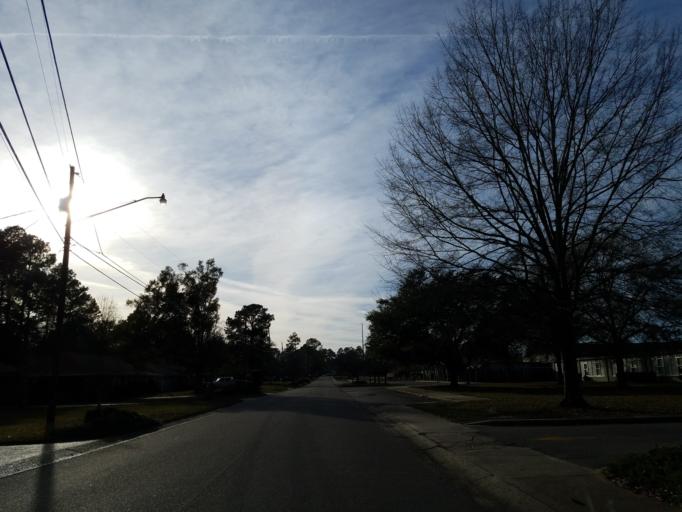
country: US
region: Mississippi
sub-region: Lamar County
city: West Hattiesburg
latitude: 31.3127
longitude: -89.3356
